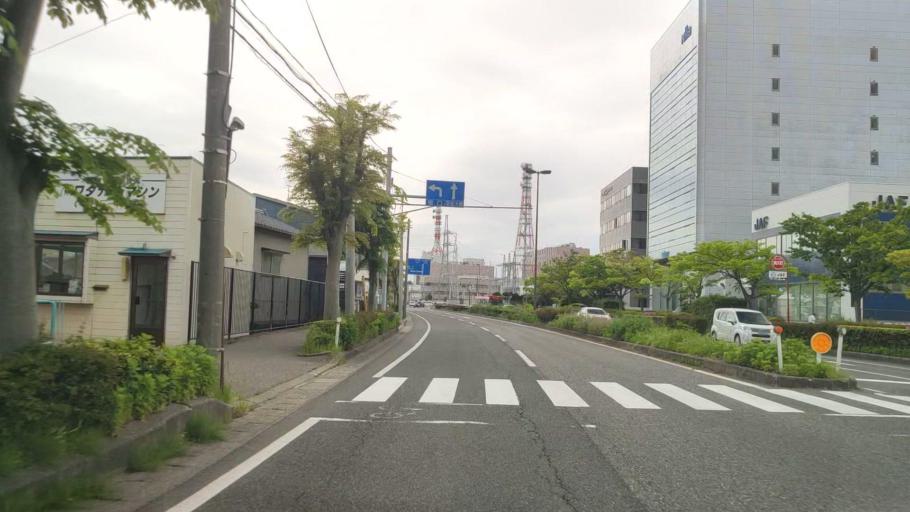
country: JP
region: Niigata
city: Niigata-shi
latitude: 37.8993
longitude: 139.0223
